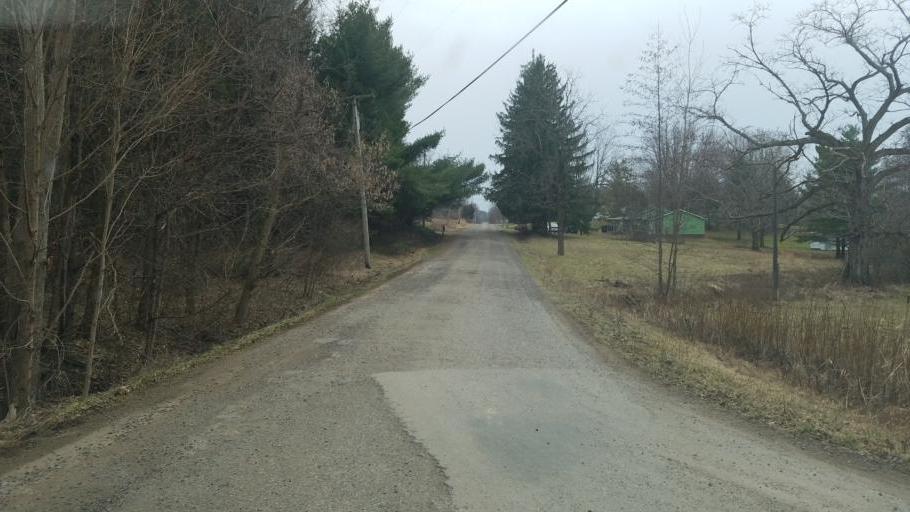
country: US
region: Ohio
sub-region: Crawford County
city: Galion
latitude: 40.6614
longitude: -82.7940
